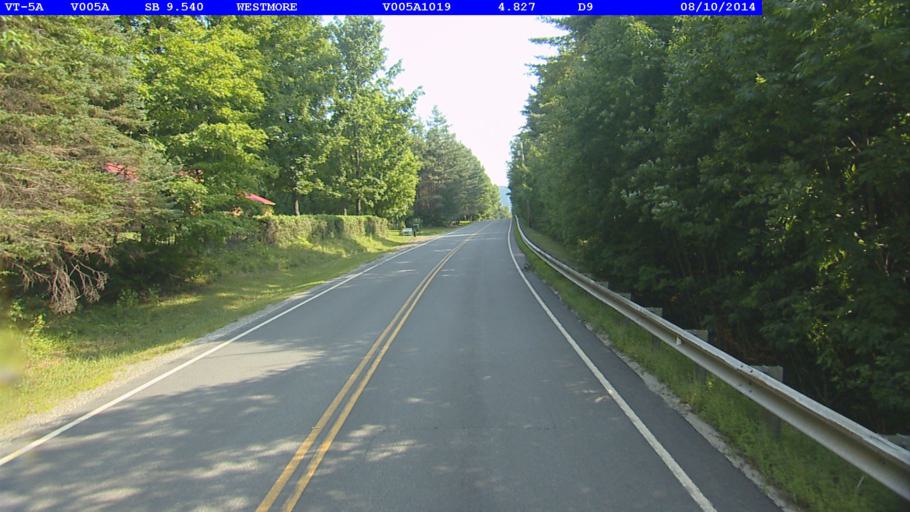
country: US
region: Vermont
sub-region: Caledonia County
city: Lyndonville
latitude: 44.7600
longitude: -72.0523
